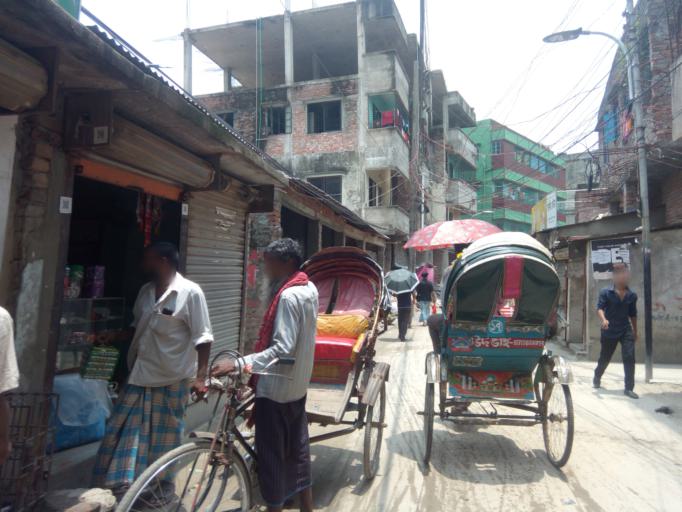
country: BD
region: Dhaka
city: Paltan
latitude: 23.7560
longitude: 90.4321
